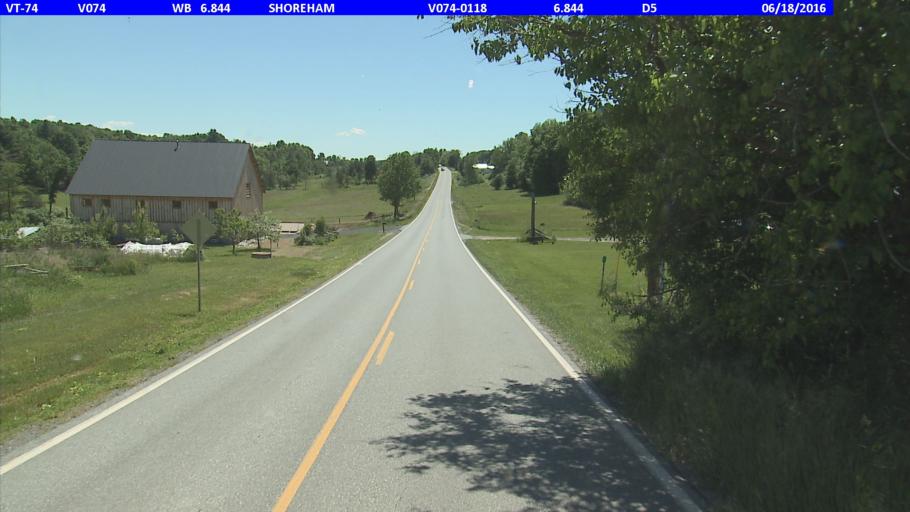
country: US
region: New York
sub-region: Essex County
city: Ticonderoga
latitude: 43.9182
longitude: -73.2954
